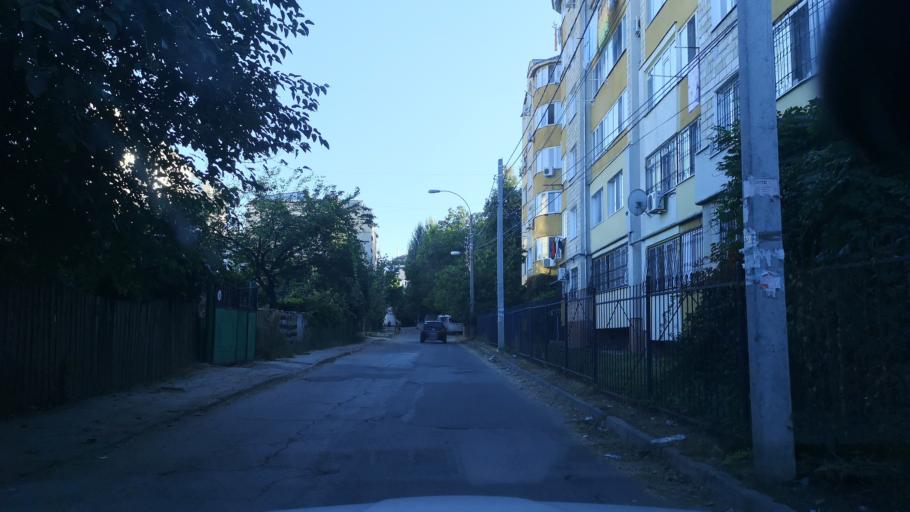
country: MD
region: Chisinau
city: Chisinau
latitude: 46.9889
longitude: 28.8754
